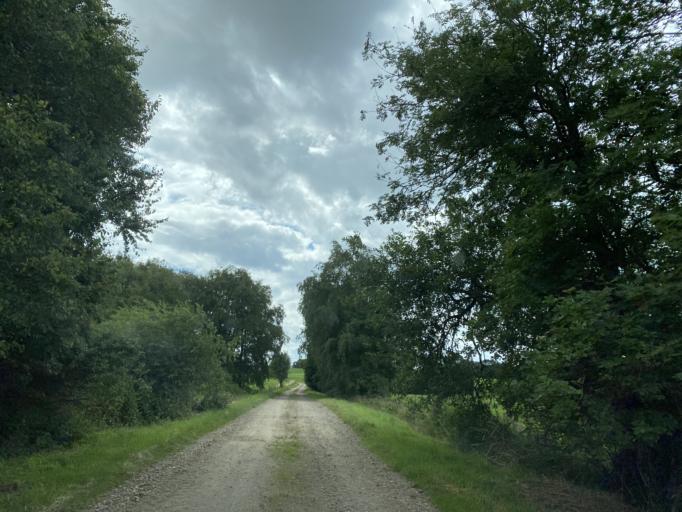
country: DK
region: Central Jutland
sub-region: Silkeborg Kommune
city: Silkeborg
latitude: 56.2168
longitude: 9.5706
